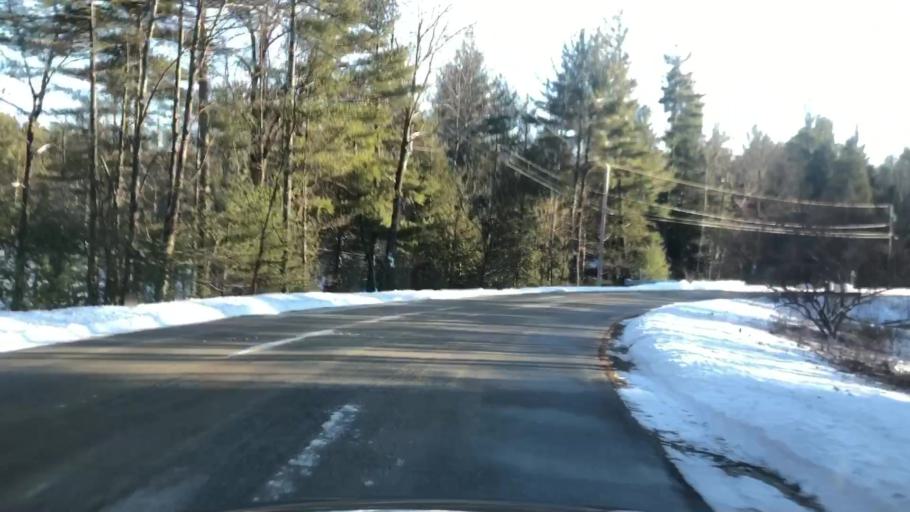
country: US
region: New Hampshire
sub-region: Hillsborough County
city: Milford
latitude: 42.7968
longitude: -71.6643
